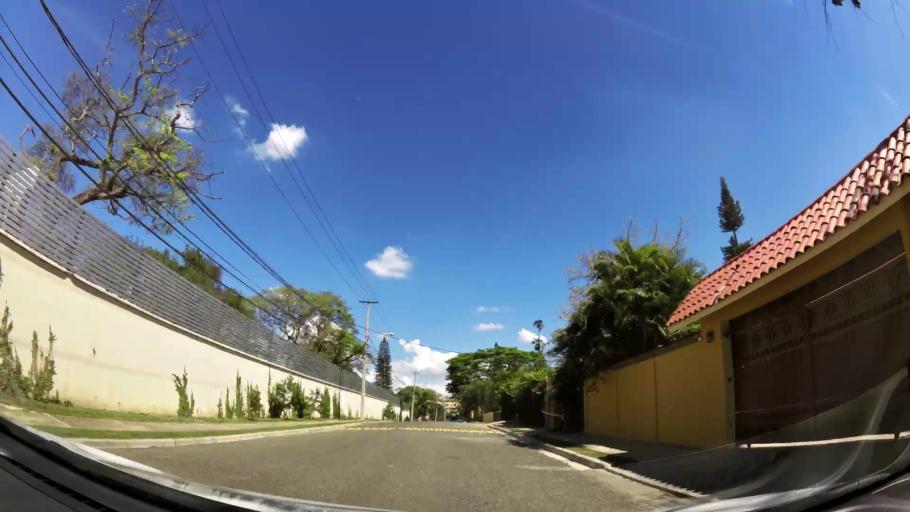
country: DO
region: Santiago
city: Santiago de los Caballeros
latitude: 19.4523
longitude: -70.6875
